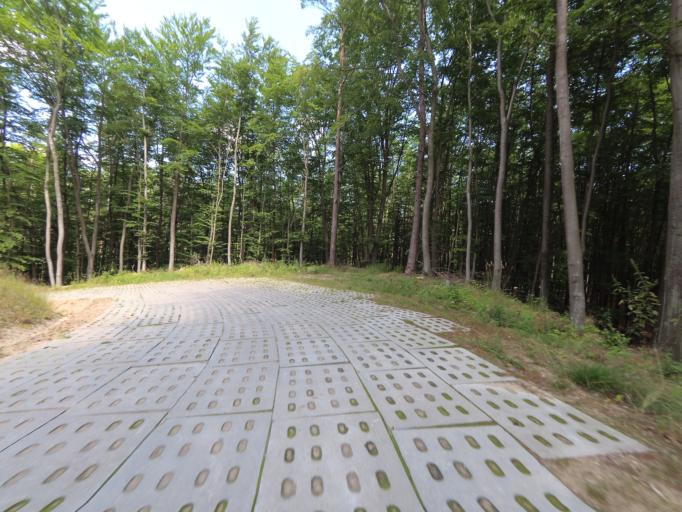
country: PL
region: Pomeranian Voivodeship
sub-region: Gdynia
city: Wielki Kack
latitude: 54.4833
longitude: 18.5029
